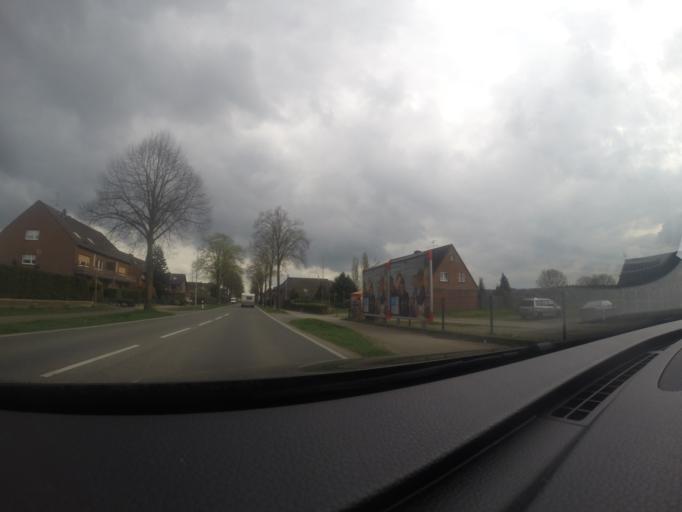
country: DE
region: North Rhine-Westphalia
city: Rees
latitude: 51.7009
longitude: 6.3722
